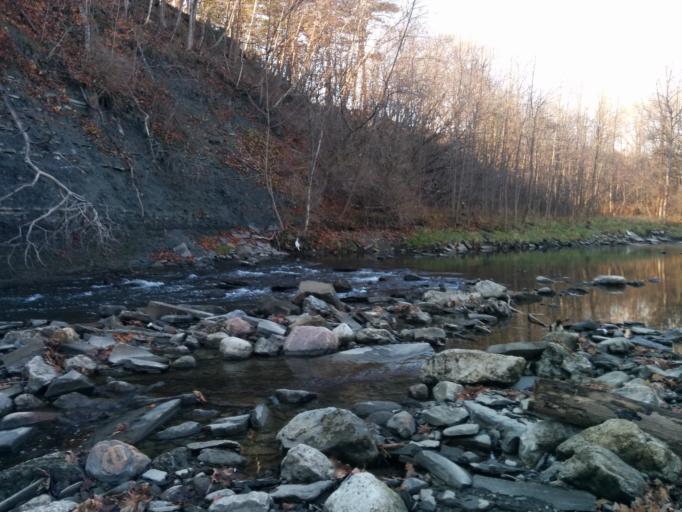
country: CA
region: Ontario
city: Etobicoke
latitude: 43.5957
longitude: -79.5537
